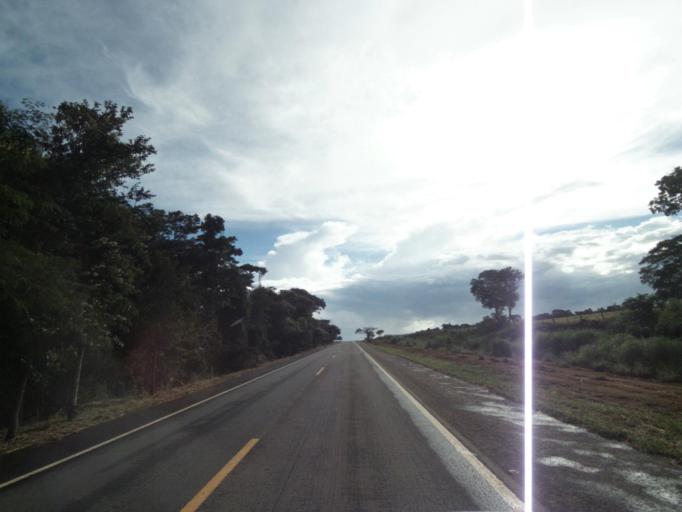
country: BR
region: Goias
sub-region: Itaberai
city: Itaberai
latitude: -15.9795
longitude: -49.6856
